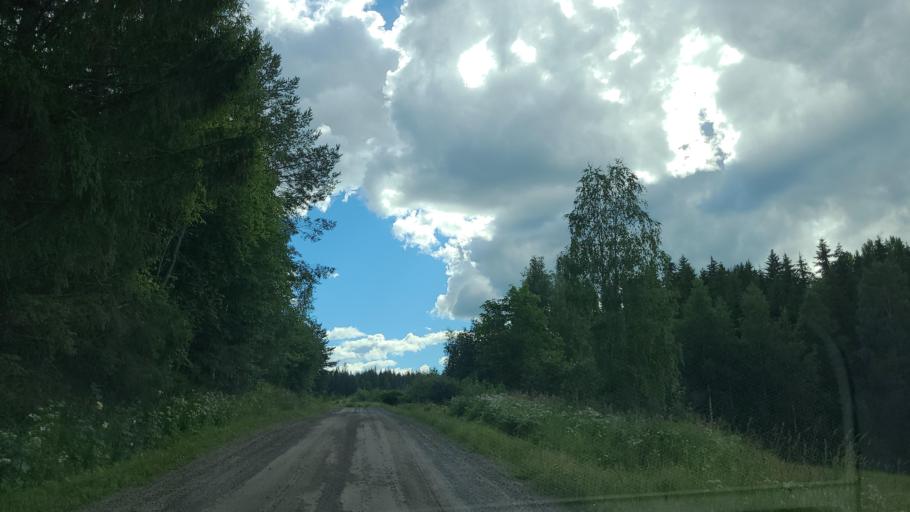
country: FI
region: Central Finland
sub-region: Jaemsae
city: Jaemsae
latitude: 61.9326
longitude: 25.3291
